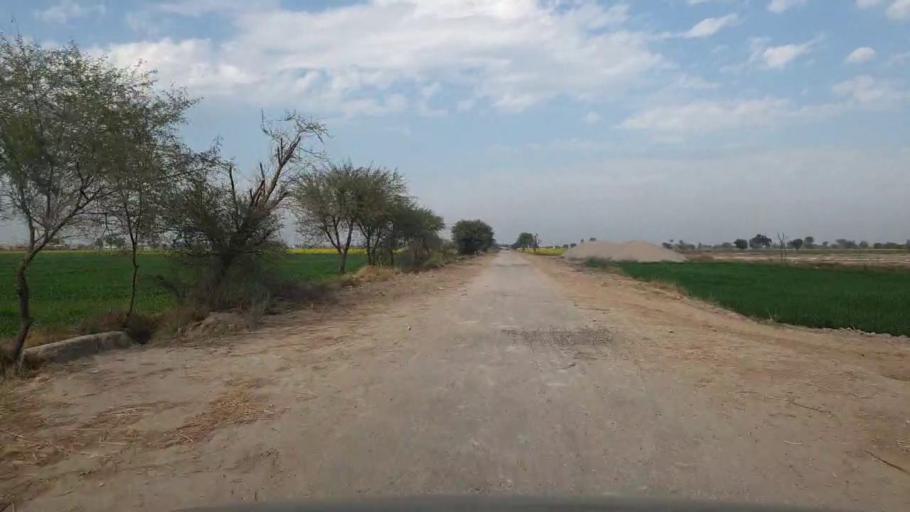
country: PK
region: Sindh
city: Hala
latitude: 26.0026
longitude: 68.4147
